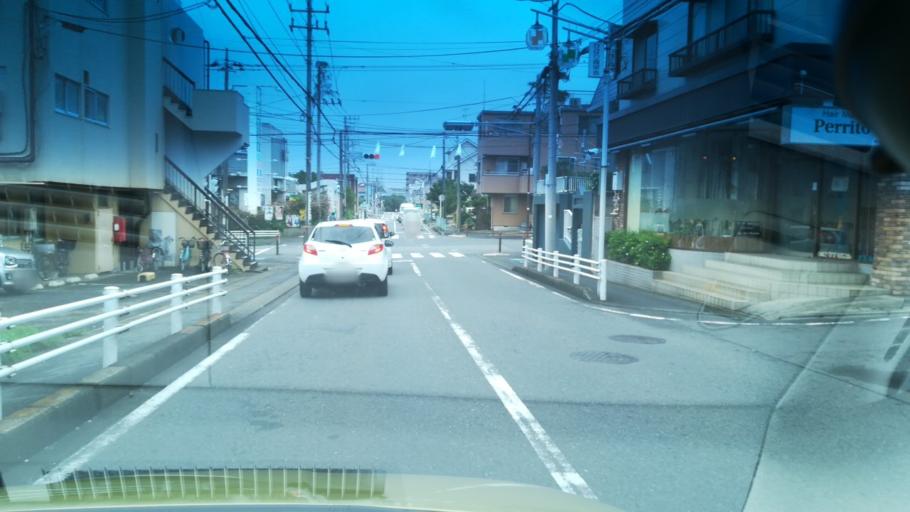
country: JP
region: Kanagawa
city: Zama
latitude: 35.5617
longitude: 139.3678
